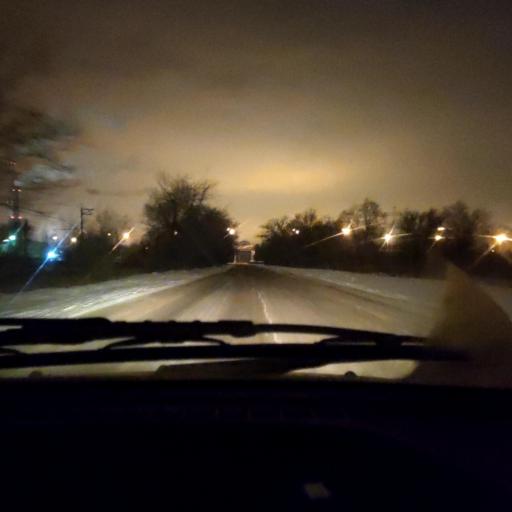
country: RU
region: Samara
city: Zhigulevsk
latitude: 53.4852
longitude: 49.5029
